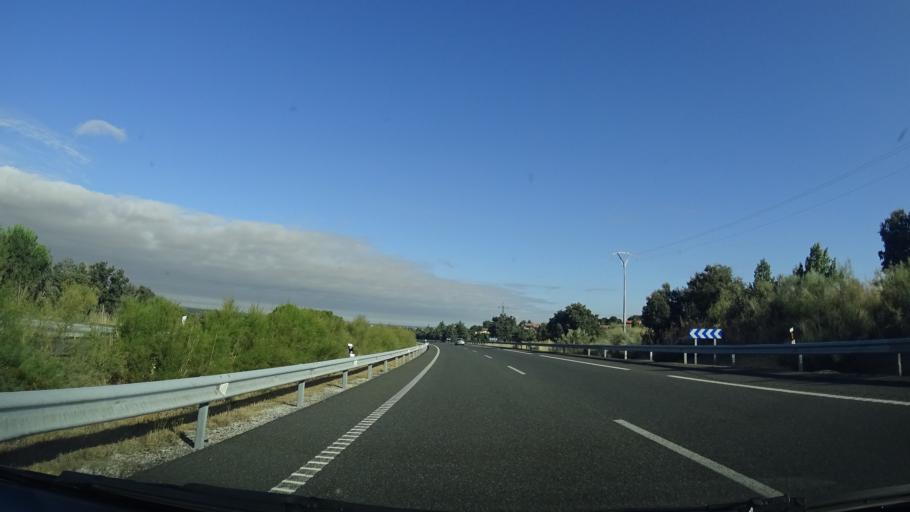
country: ES
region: Castille and Leon
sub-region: Provincia de Segovia
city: Labajos
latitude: 40.8545
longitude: -4.5468
